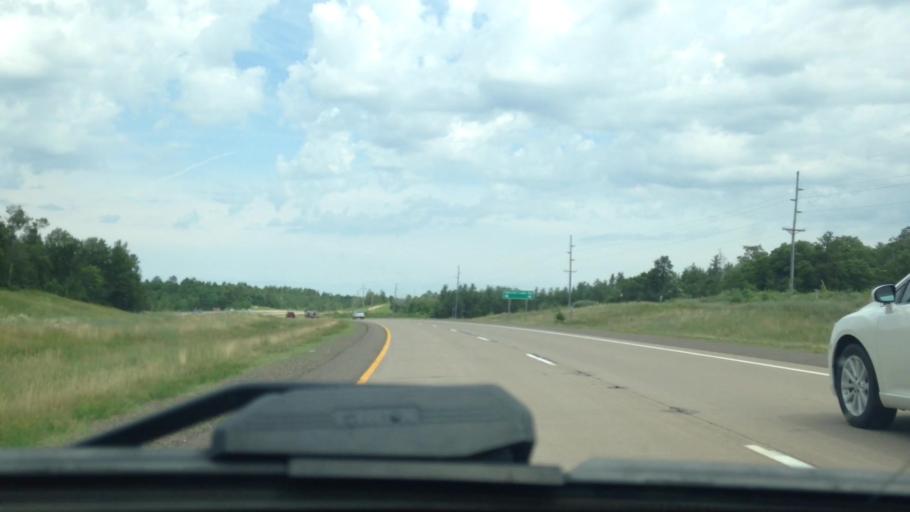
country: US
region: Wisconsin
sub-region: Douglas County
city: Lake Nebagamon
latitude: 46.2140
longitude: -91.7967
